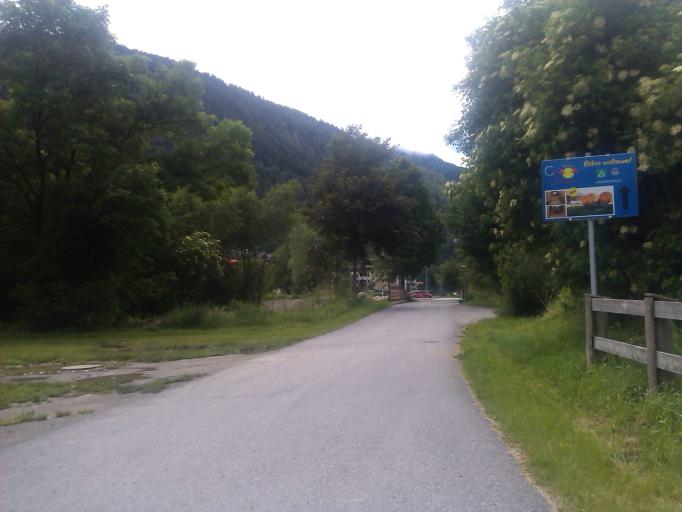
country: AT
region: Tyrol
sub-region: Politischer Bezirk Landeck
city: Fendels
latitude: 47.0613
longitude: 10.6586
